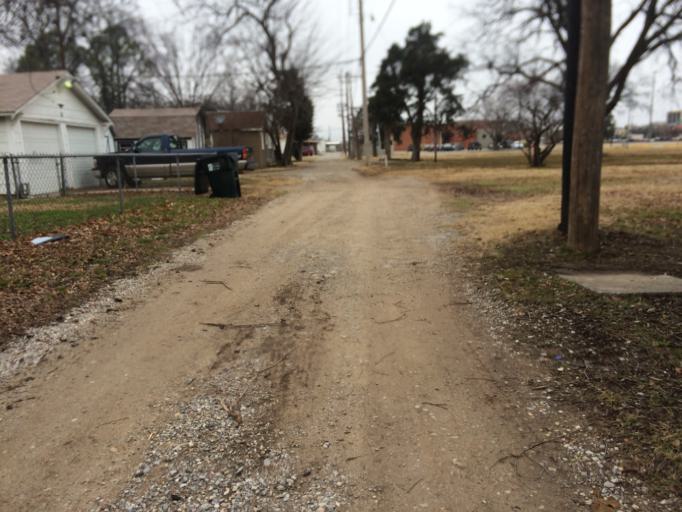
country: US
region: Oklahoma
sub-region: Cleveland County
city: Norman
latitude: 35.2169
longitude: -97.4423
